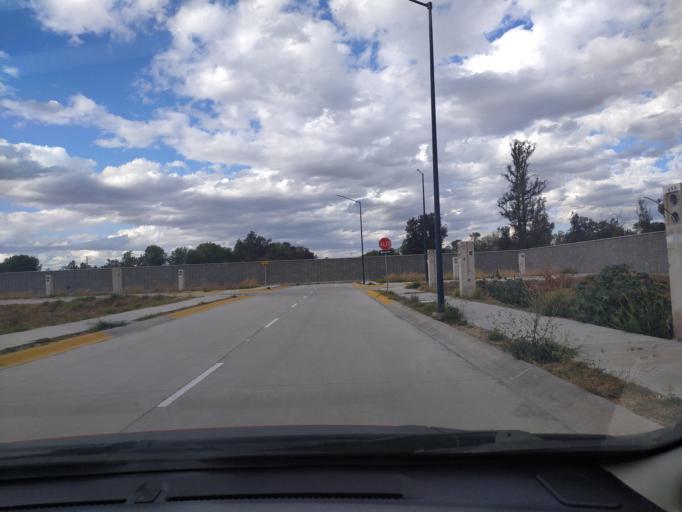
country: LA
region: Oudomxai
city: Muang La
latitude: 21.0254
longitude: 101.8196
